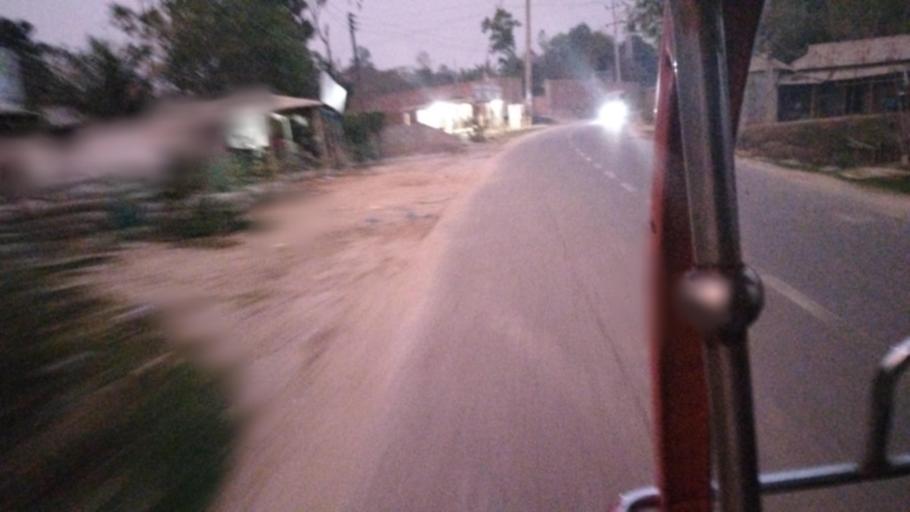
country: BD
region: Dhaka
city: Sakhipur
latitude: 24.3954
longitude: 90.3344
